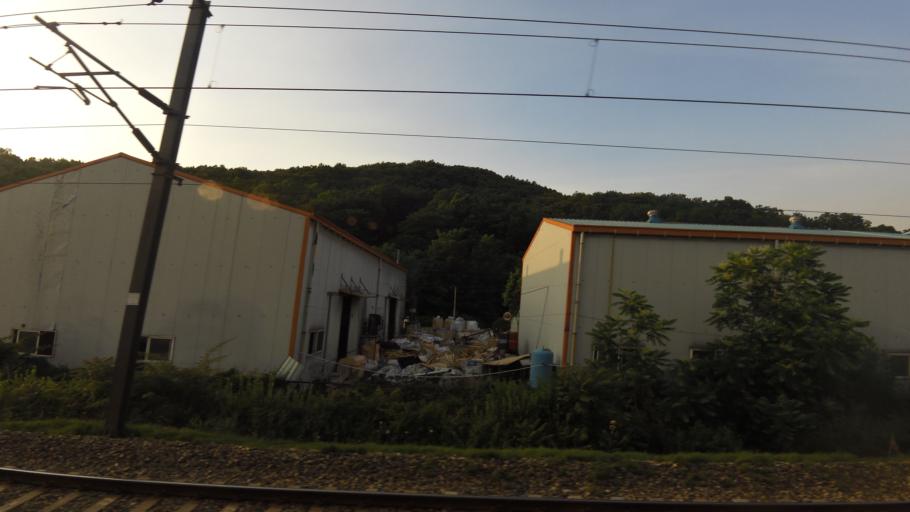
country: KR
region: Chungcheongnam-do
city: Cheonan
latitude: 36.6652
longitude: 127.2511
